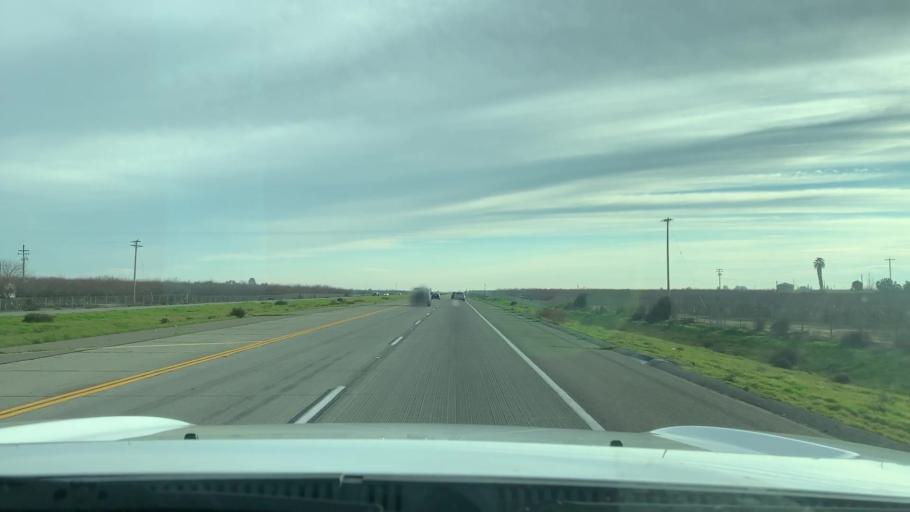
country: US
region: California
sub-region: Fresno County
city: Caruthers
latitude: 36.5439
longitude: -119.7864
